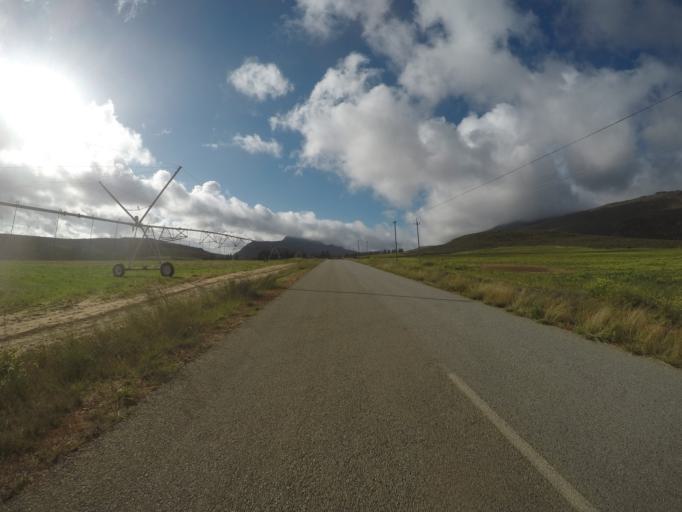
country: ZA
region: Western Cape
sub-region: West Coast District Municipality
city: Clanwilliam
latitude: -32.3440
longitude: 18.8394
